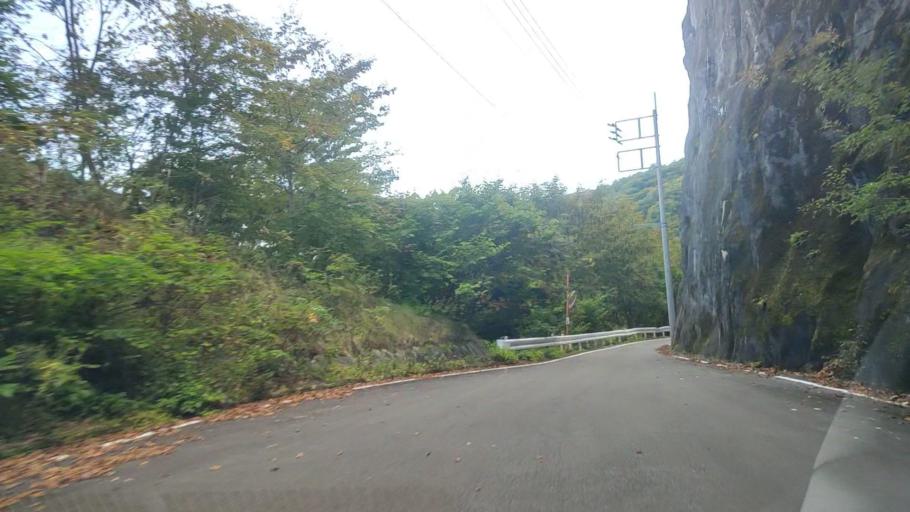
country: JP
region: Gunma
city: Nakanojomachi
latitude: 36.6515
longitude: 138.6189
